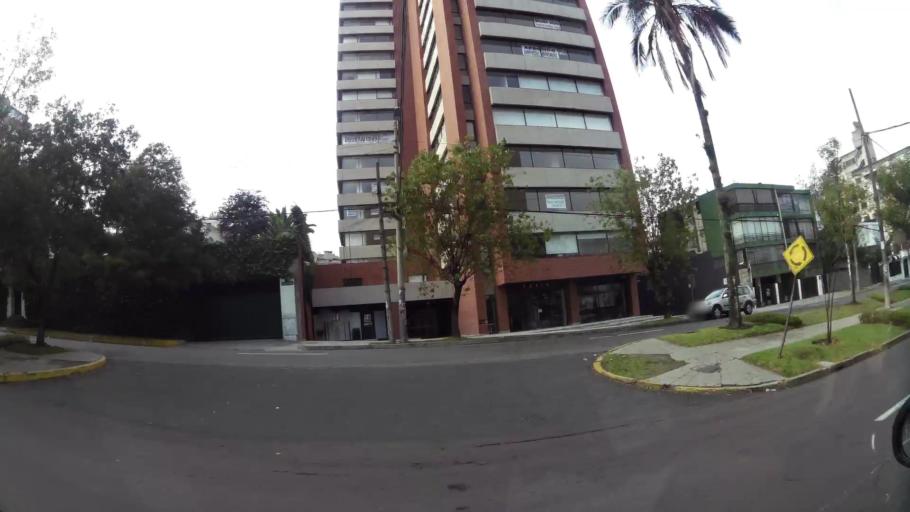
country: EC
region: Pichincha
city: Quito
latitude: -0.2029
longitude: -78.4819
